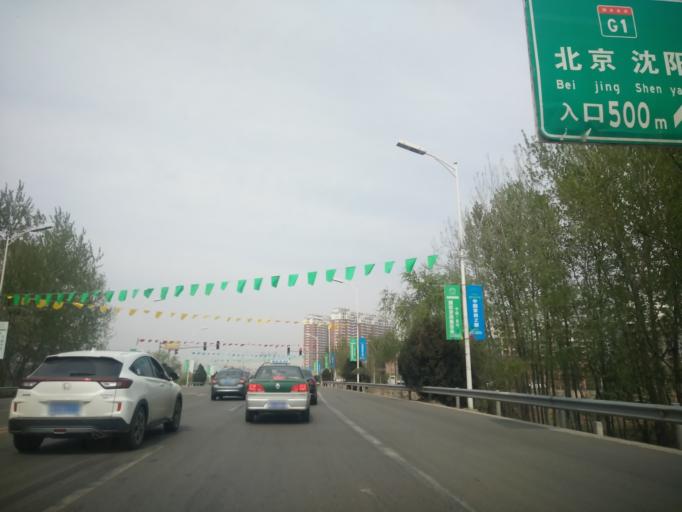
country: CN
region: Beijing
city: Xiji
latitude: 39.7850
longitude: 116.9872
